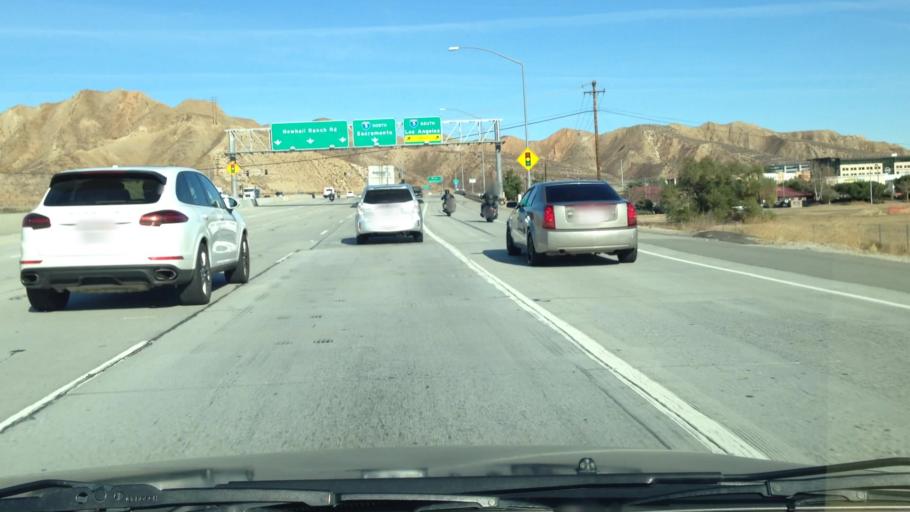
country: US
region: California
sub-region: Los Angeles County
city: Valencia
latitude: 34.4407
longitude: -118.6093
